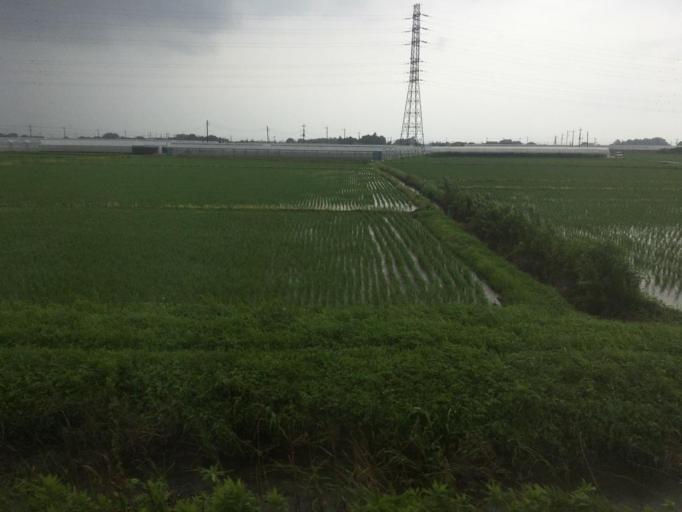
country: JP
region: Tochigi
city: Ashikaga
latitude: 36.2926
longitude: 139.4696
